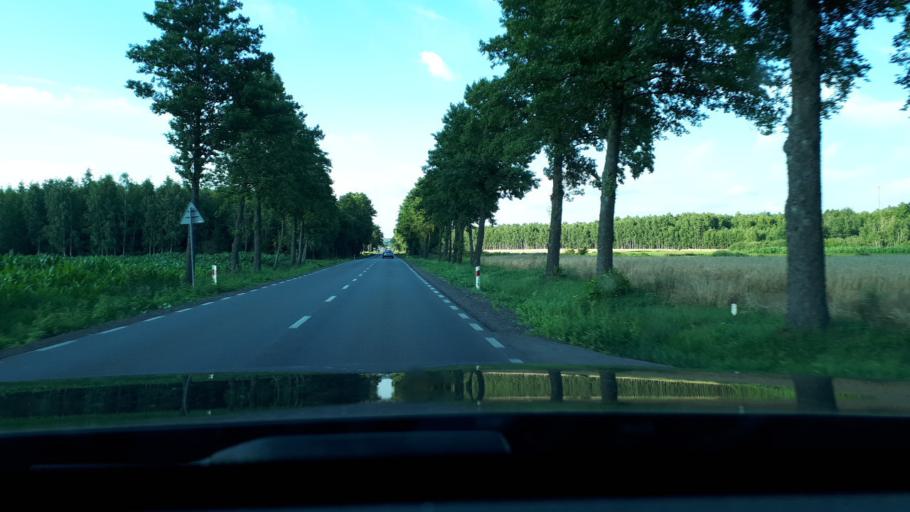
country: PL
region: Masovian Voivodeship
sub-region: Powiat ciechanowski
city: Ojrzen
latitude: 52.7550
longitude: 20.5360
